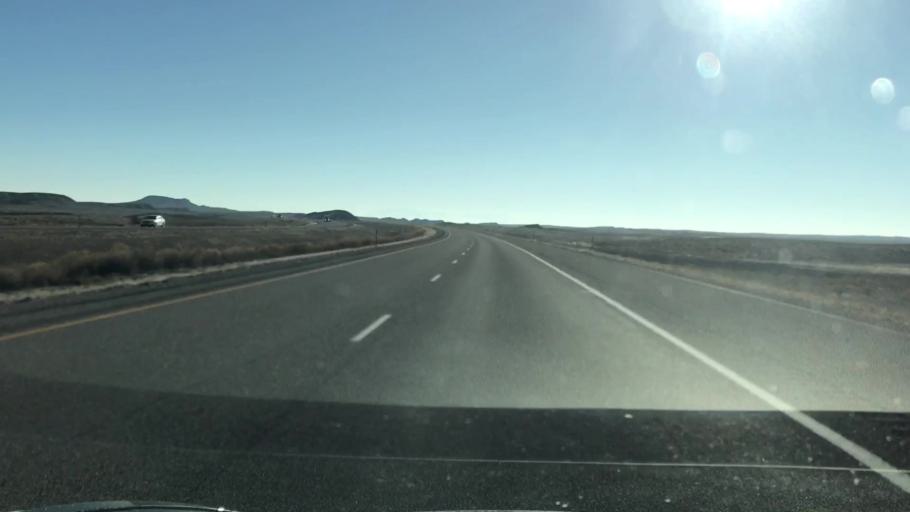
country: US
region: Utah
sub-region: Grand County
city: Moab
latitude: 38.9376
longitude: -110.0302
